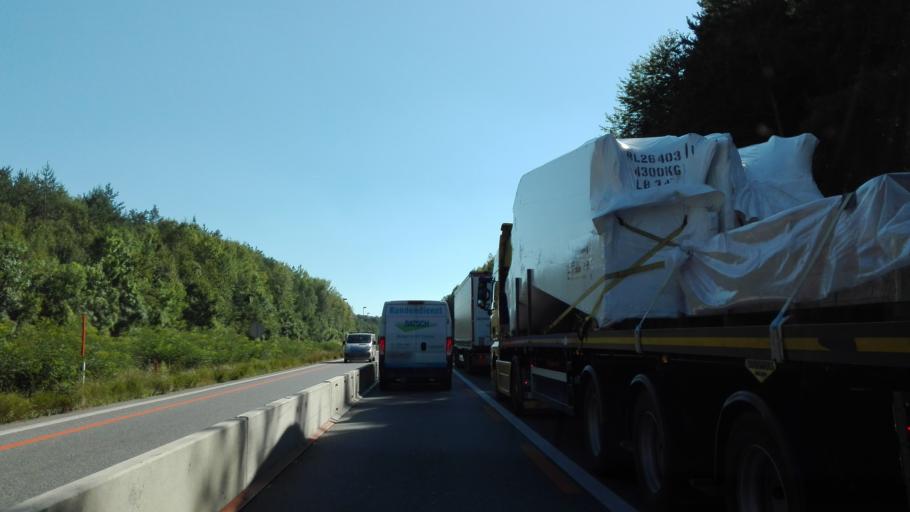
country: AT
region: Lower Austria
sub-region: Politischer Bezirk Modling
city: Gaaden
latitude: 48.0664
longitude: 16.1670
